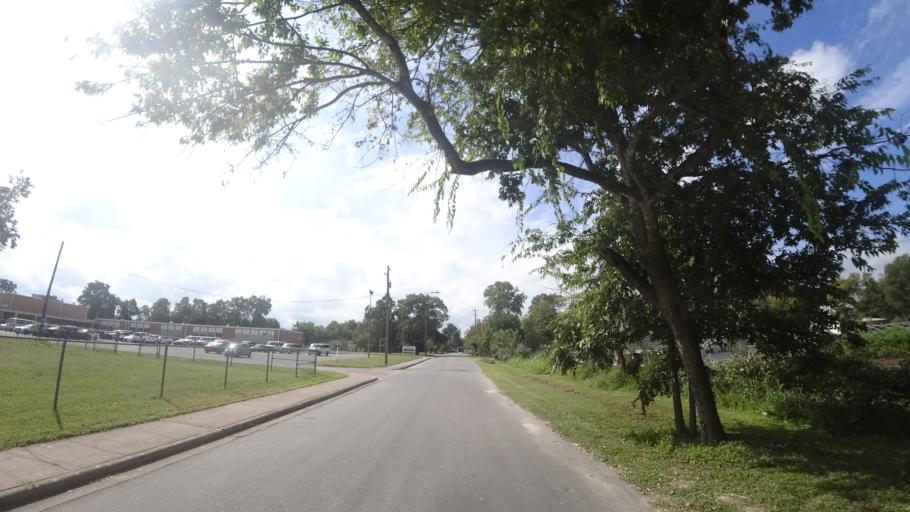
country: US
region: Texas
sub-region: Travis County
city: Austin
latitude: 30.2572
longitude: -97.6983
